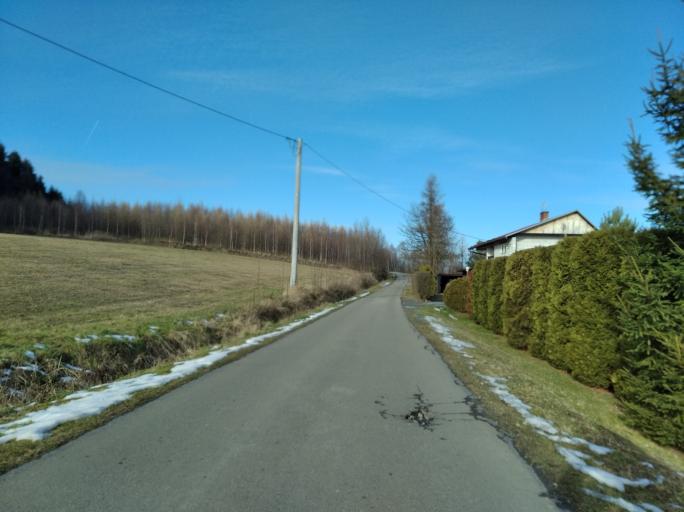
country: PL
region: Subcarpathian Voivodeship
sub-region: Powiat strzyzowski
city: Gwoznica Gorna
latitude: 49.8173
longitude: 21.9900
